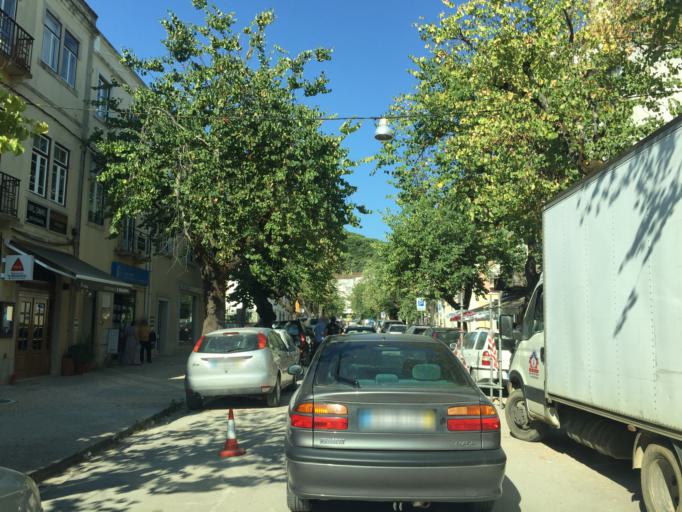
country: PT
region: Santarem
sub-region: Tomar
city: Tomar
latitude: 39.6017
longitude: -8.4135
